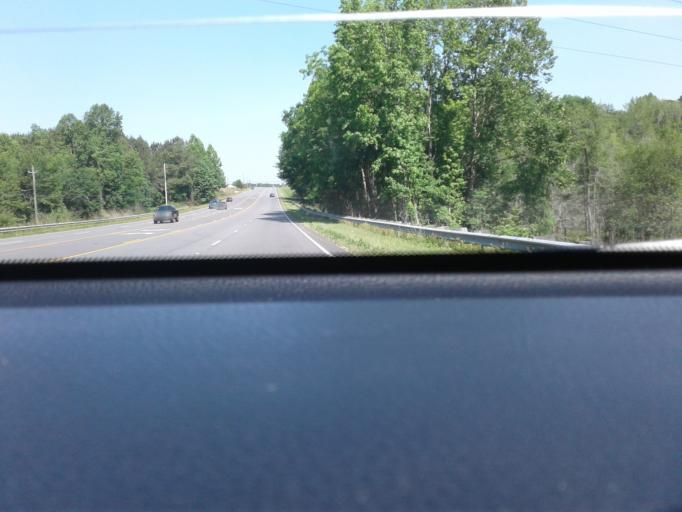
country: US
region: North Carolina
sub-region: Harnett County
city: Buies Creek
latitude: 35.3817
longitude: -78.7174
